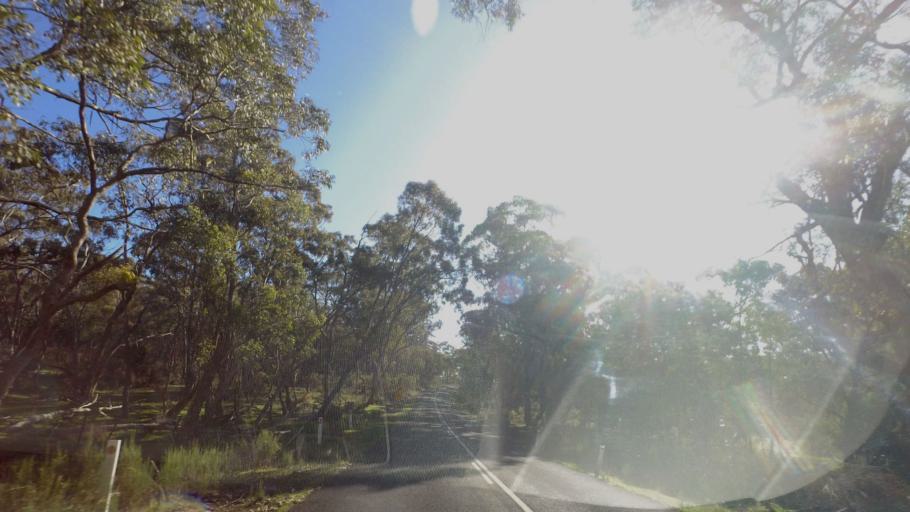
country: AU
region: Victoria
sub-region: Greater Bendigo
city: Kangaroo Flat
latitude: -36.8844
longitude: 144.2846
